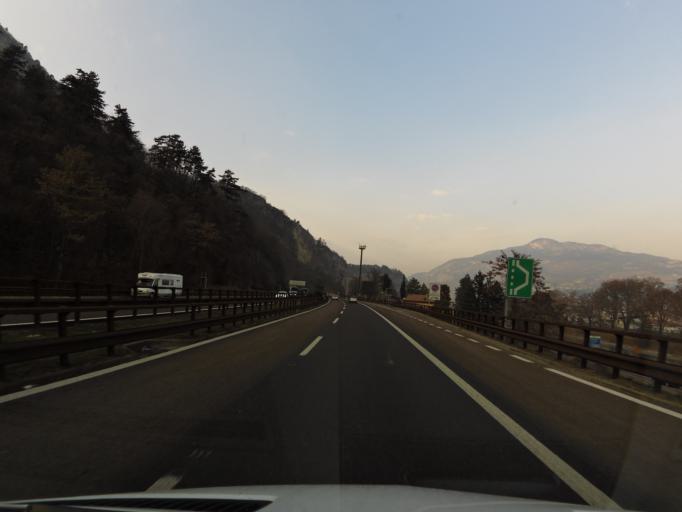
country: IT
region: Trentino-Alto Adige
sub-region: Provincia di Trento
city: Trento
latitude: 46.0619
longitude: 11.1104
